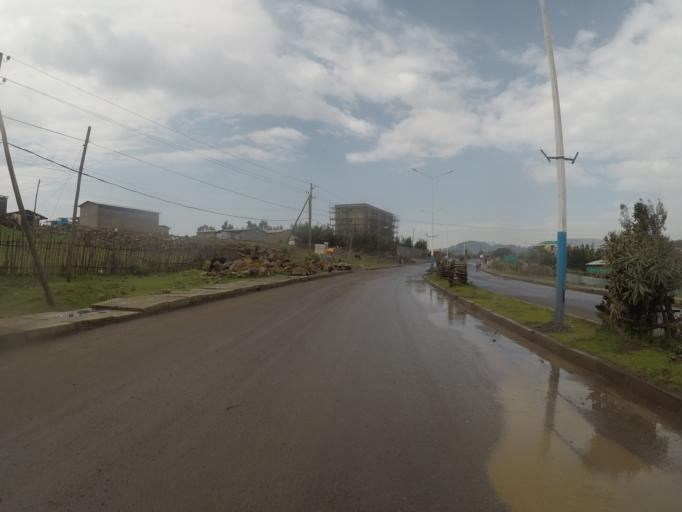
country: ET
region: Amhara
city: Debark'
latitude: 13.1440
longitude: 37.8937
